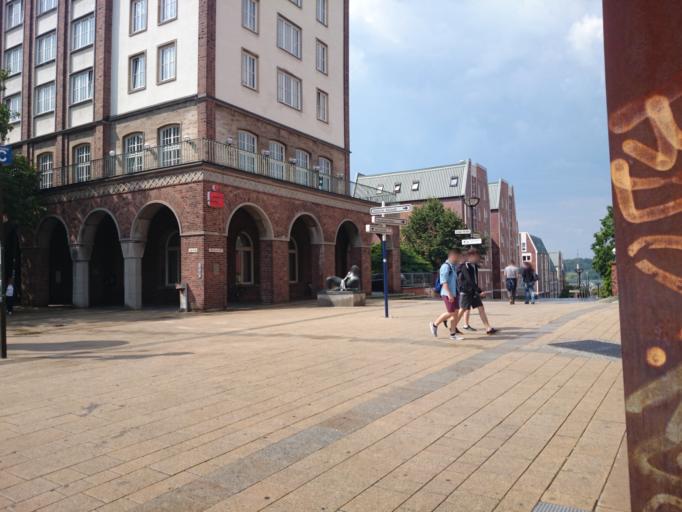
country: DE
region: Mecklenburg-Vorpommern
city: Rostock
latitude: 54.0900
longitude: 12.1345
